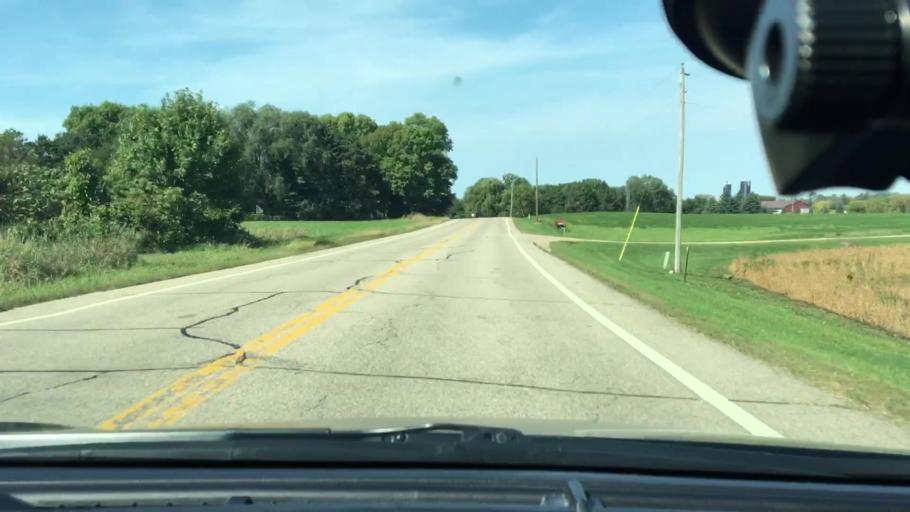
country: US
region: Minnesota
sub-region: Hennepin County
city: Corcoran
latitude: 45.1193
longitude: -93.5998
